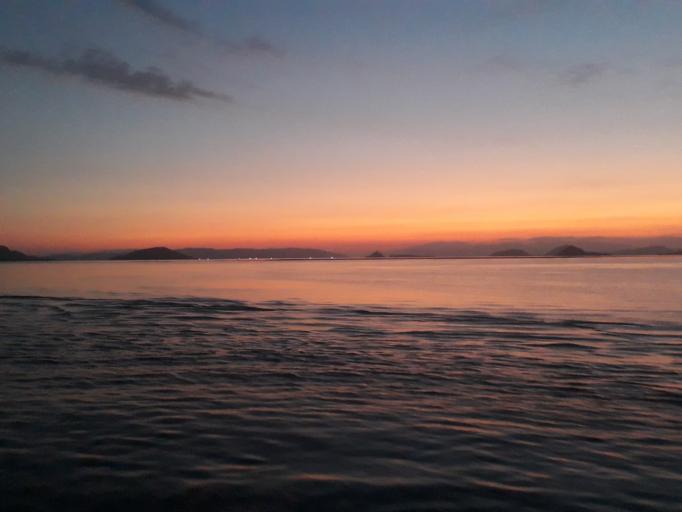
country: ID
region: East Nusa Tenggara
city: Mesa
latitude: -8.6021
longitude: 119.7652
